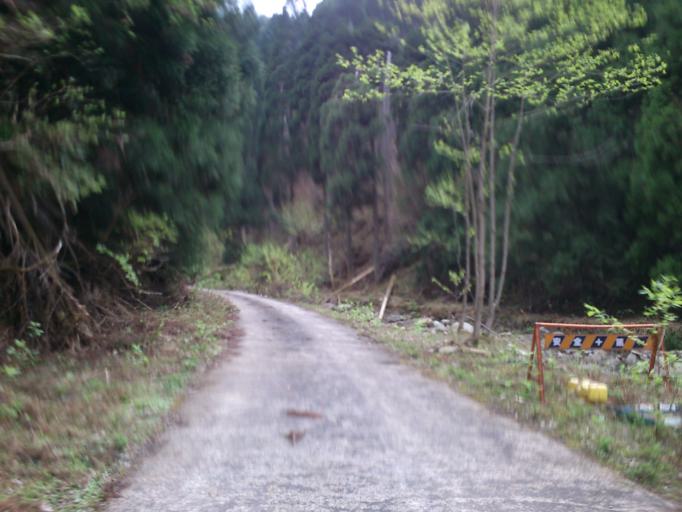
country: JP
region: Kyoto
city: Maizuru
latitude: 35.4061
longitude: 135.5114
